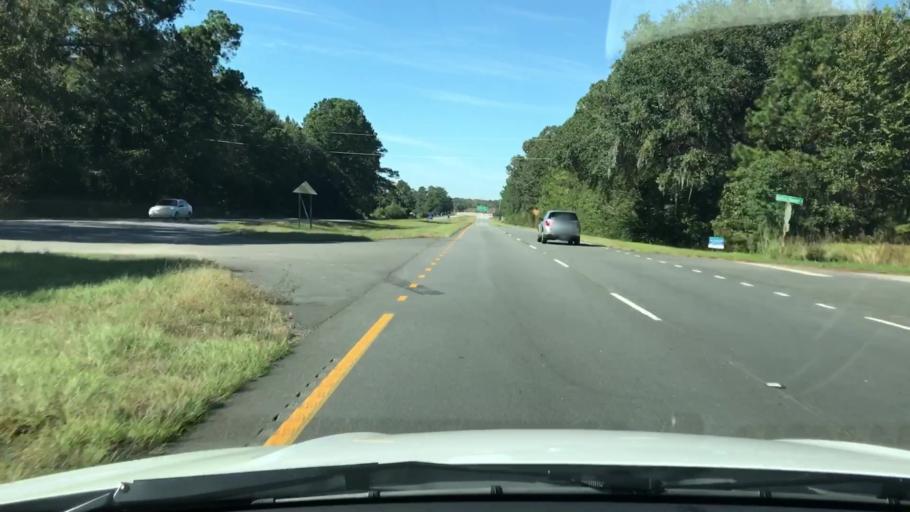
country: US
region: South Carolina
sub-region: Hampton County
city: Yemassee
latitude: 32.5939
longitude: -80.7519
